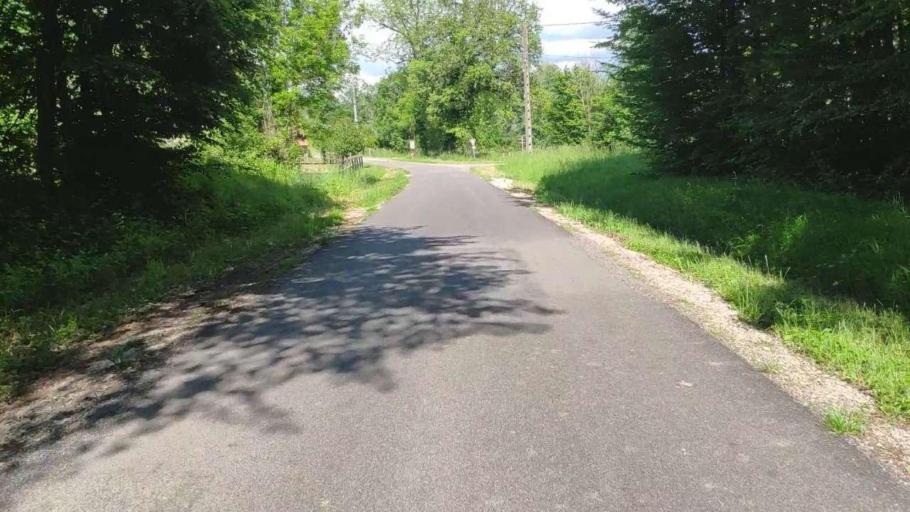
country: FR
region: Franche-Comte
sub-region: Departement du Jura
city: Bletterans
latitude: 46.8026
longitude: 5.4259
